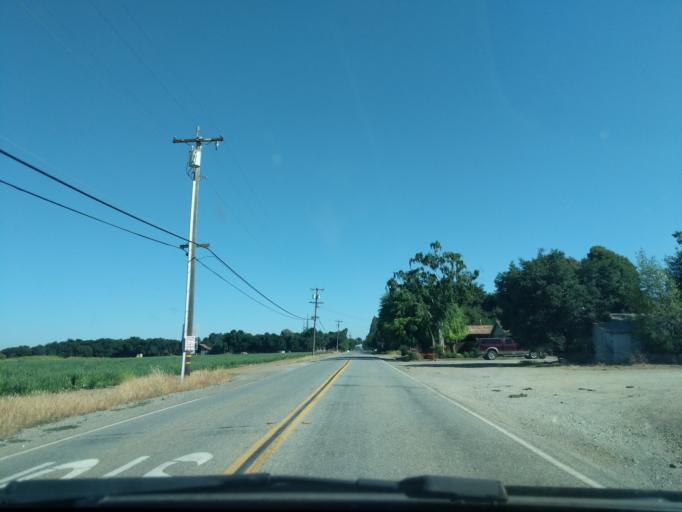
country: US
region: California
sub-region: Santa Clara County
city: Gilroy
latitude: 37.0350
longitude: -121.5382
